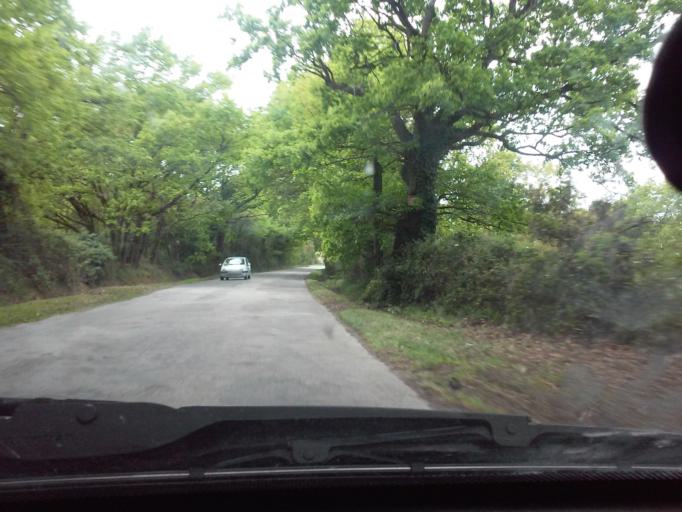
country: FR
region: Brittany
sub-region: Departement d'Ille-et-Vilaine
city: Saint-Jacques-de-la-Lande
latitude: 48.0861
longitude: -1.7335
